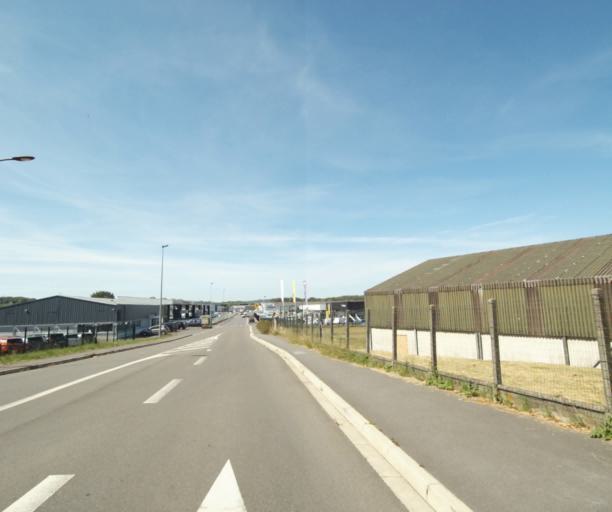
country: FR
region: Champagne-Ardenne
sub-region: Departement des Ardennes
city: Villers-Semeuse
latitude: 49.7415
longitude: 4.7390
